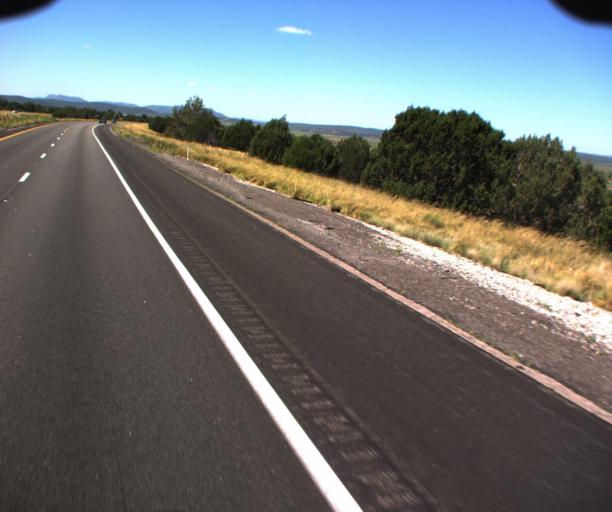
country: US
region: Arizona
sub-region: Mohave County
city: Peach Springs
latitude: 35.2817
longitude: -113.1266
